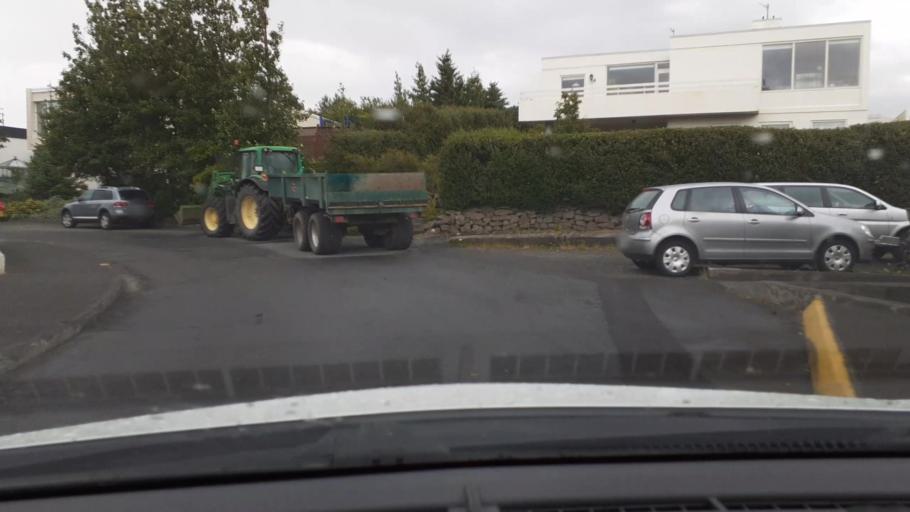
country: IS
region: West
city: Borgarnes
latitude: 64.5403
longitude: -21.9145
